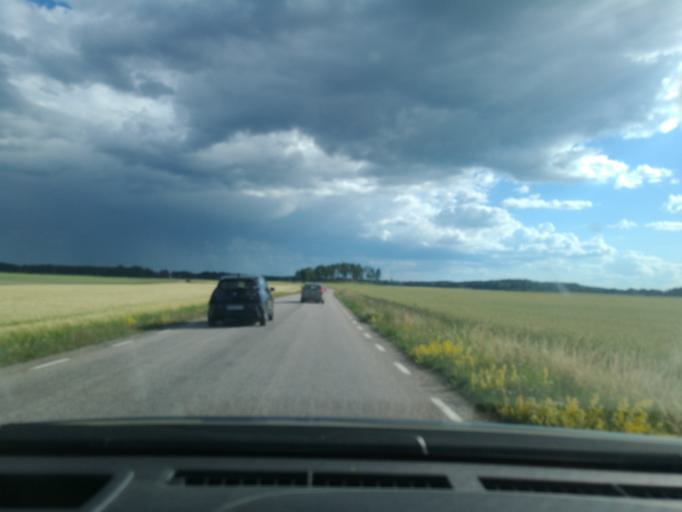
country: SE
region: Soedermanland
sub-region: Eskilstuna Kommun
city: Arla
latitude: 59.4363
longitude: 16.7126
